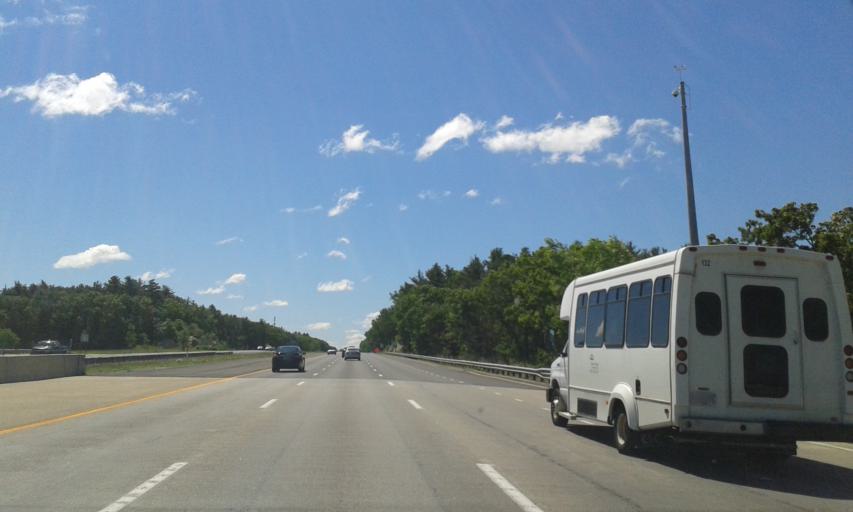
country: US
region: Massachusetts
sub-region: Middlesex County
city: Pinehurst
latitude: 42.5027
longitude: -71.2443
